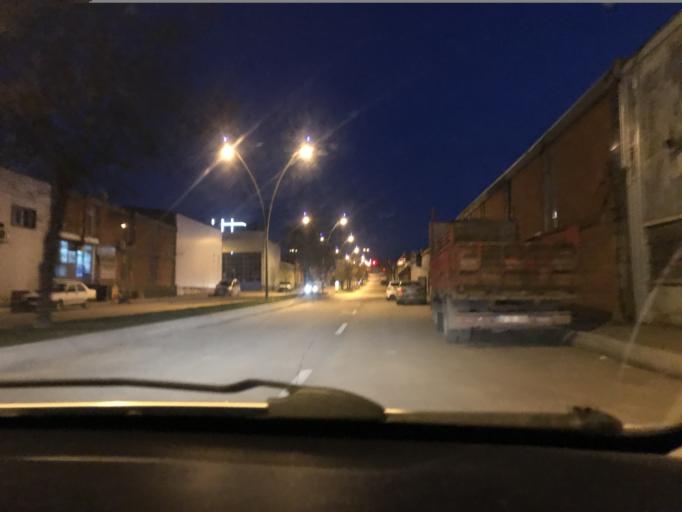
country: TR
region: Ankara
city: Batikent
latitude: 39.9726
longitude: 32.7397
